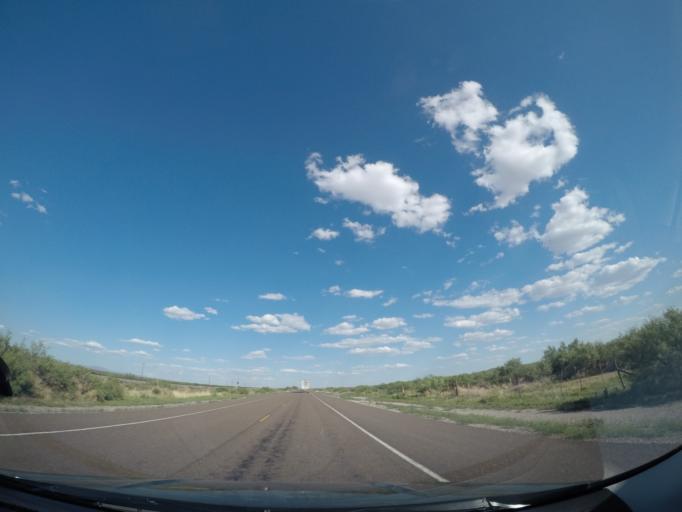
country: US
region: Texas
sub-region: Culberson County
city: Van Horn
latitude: 30.6701
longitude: -104.6027
